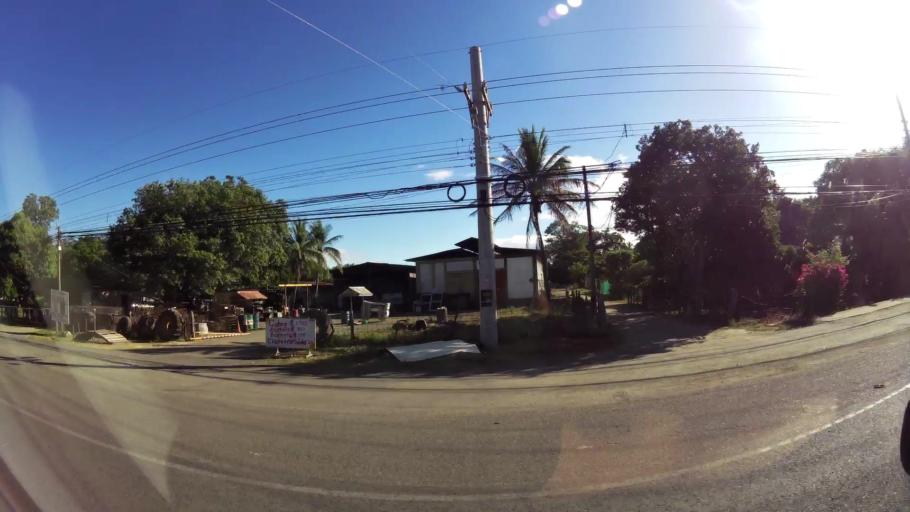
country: CR
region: Guanacaste
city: Belen
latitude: 10.4547
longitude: -85.5556
